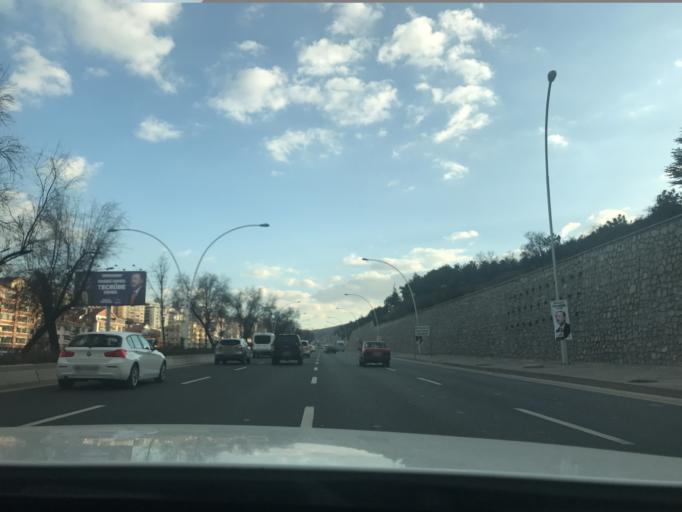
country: TR
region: Ankara
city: Ankara
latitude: 39.8789
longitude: 32.8115
